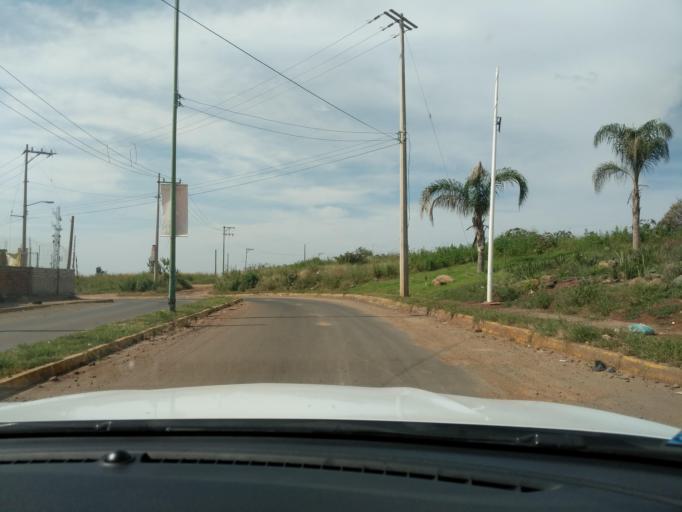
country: MX
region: Jalisco
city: San Jose del Castillo
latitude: 20.5249
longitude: -103.2308
